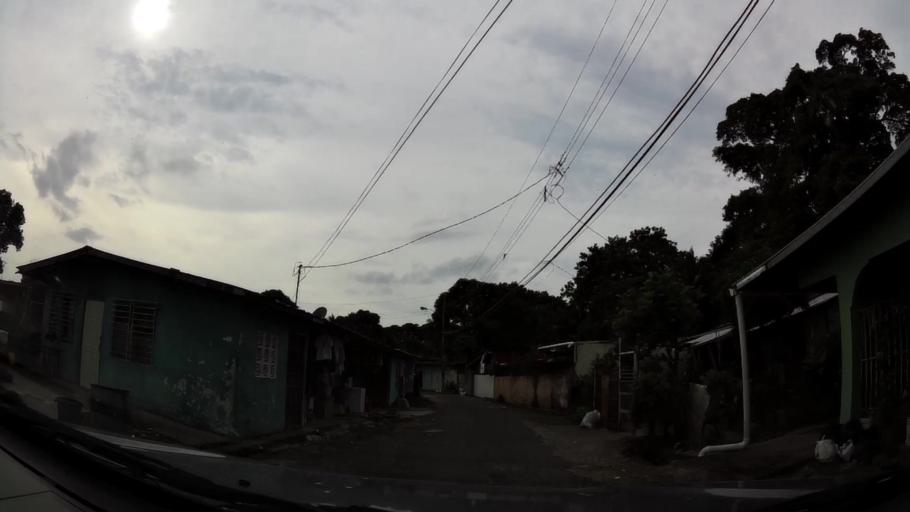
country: PA
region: Panama
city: Panama
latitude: 9.0094
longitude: -79.4853
